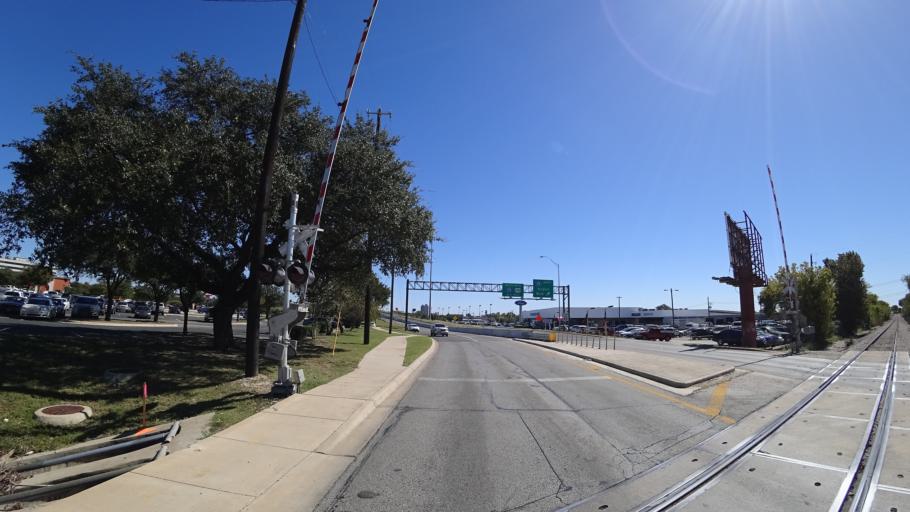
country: US
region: Texas
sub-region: Travis County
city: Austin
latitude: 30.3208
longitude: -97.7159
